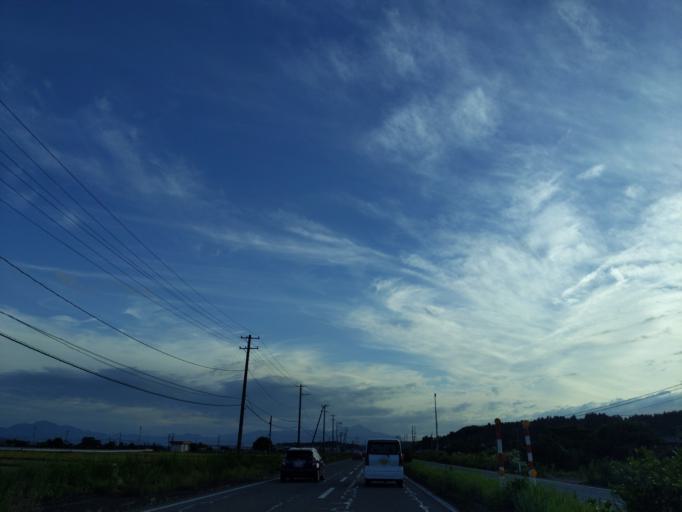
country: JP
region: Niigata
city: Kashiwazaki
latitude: 37.4413
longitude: 138.6311
